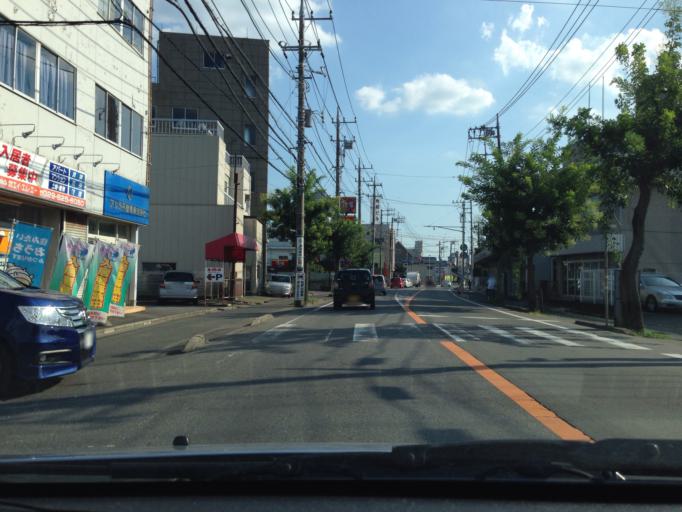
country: JP
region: Ibaraki
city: Ami
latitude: 36.0854
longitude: 140.2059
